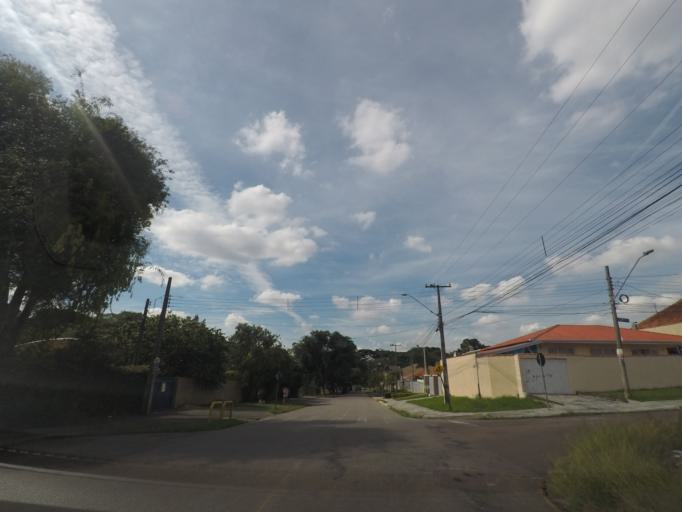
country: BR
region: Parana
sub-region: Sao Jose Dos Pinhais
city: Sao Jose dos Pinhais
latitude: -25.4920
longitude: -49.2611
